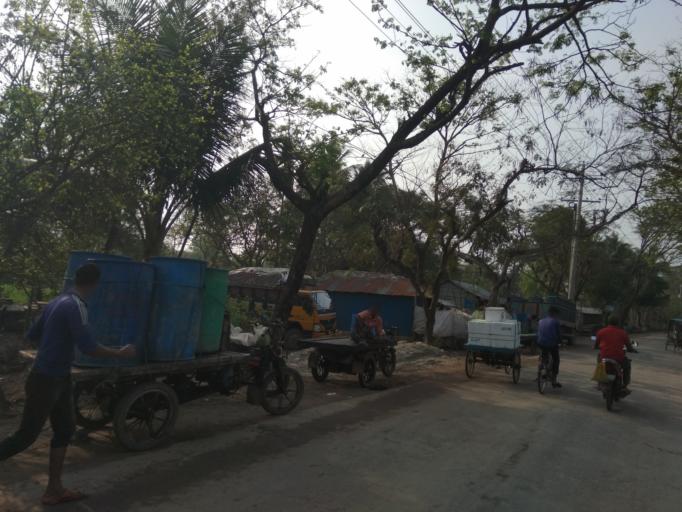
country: IN
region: West Bengal
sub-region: North 24 Parganas
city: Taki
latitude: 22.3170
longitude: 89.1062
